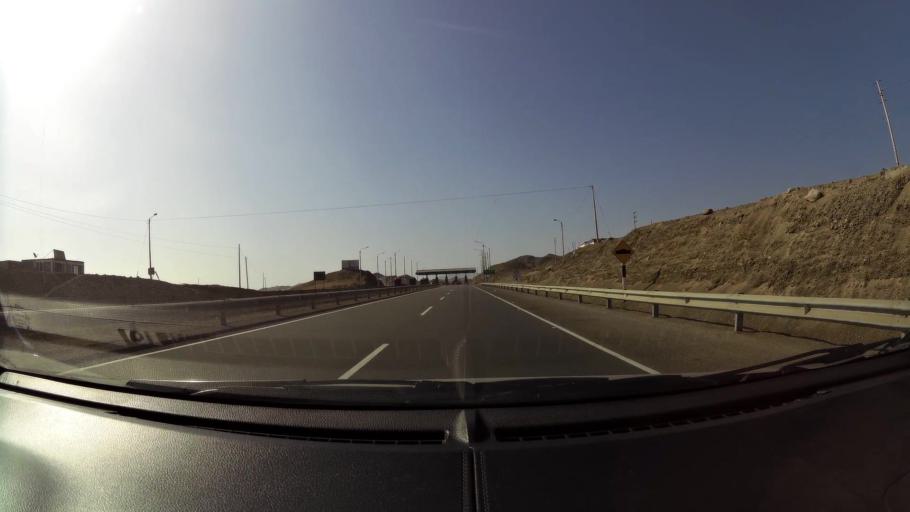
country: PE
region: Ancash
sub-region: Provincia de Huarmey
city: La Caleta Culebras
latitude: -9.9260
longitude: -78.2199
